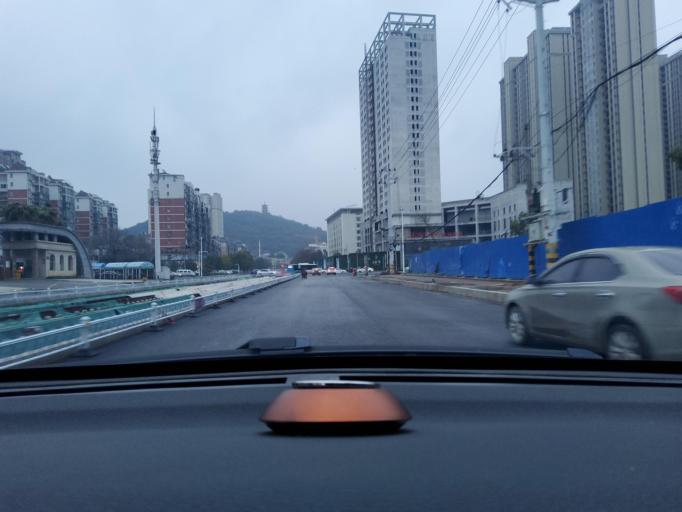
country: CN
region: Hubei
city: Tuanchengshan
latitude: 30.1950
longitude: 115.0141
